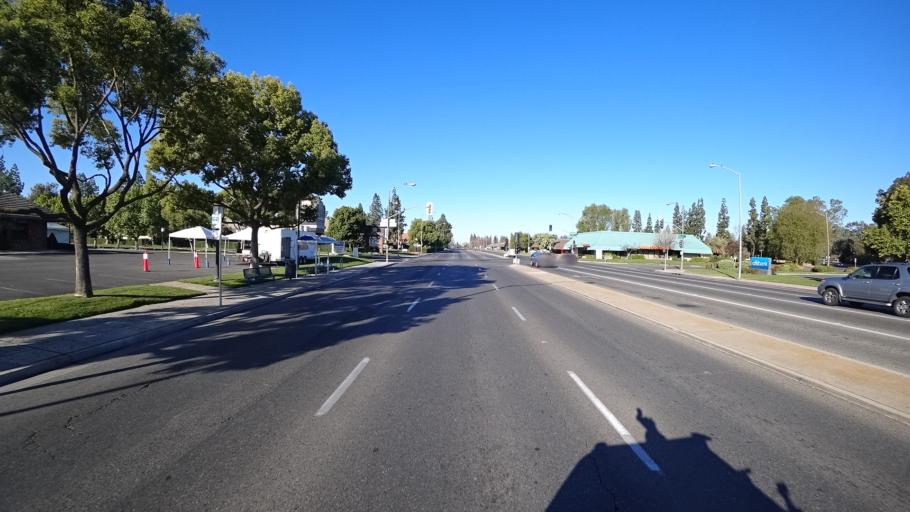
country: US
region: California
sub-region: Fresno County
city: Fresno
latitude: 36.8082
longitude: -119.8320
